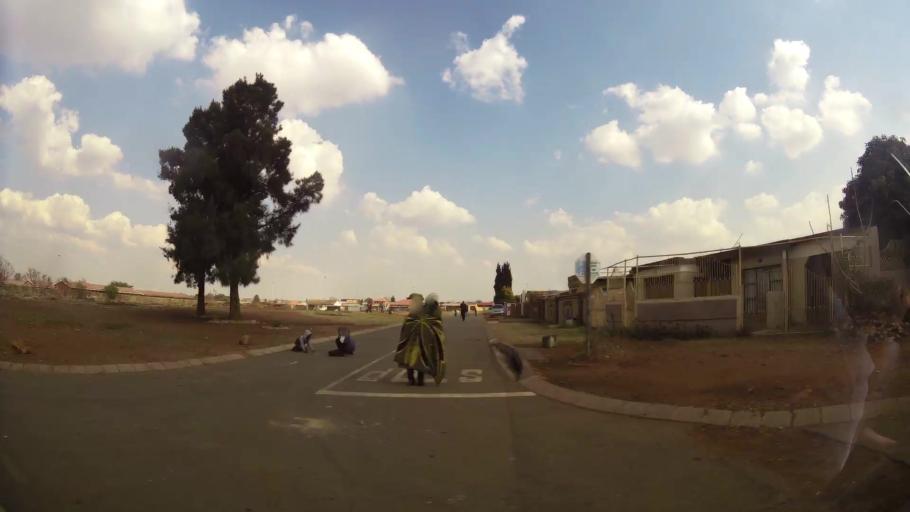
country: ZA
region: Gauteng
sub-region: Ekurhuleni Metropolitan Municipality
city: Germiston
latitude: -26.3472
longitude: 28.1589
